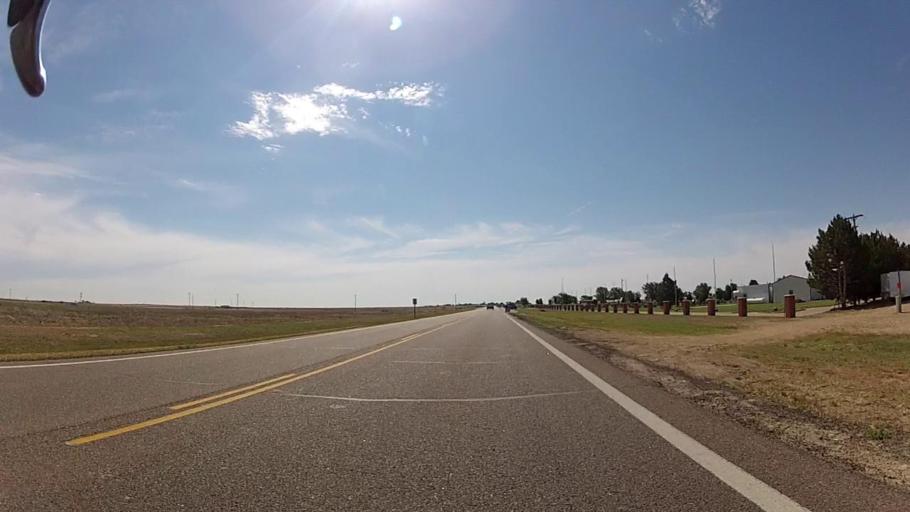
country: US
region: Kansas
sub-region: Grant County
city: Ulysses
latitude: 37.5654
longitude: -101.3138
